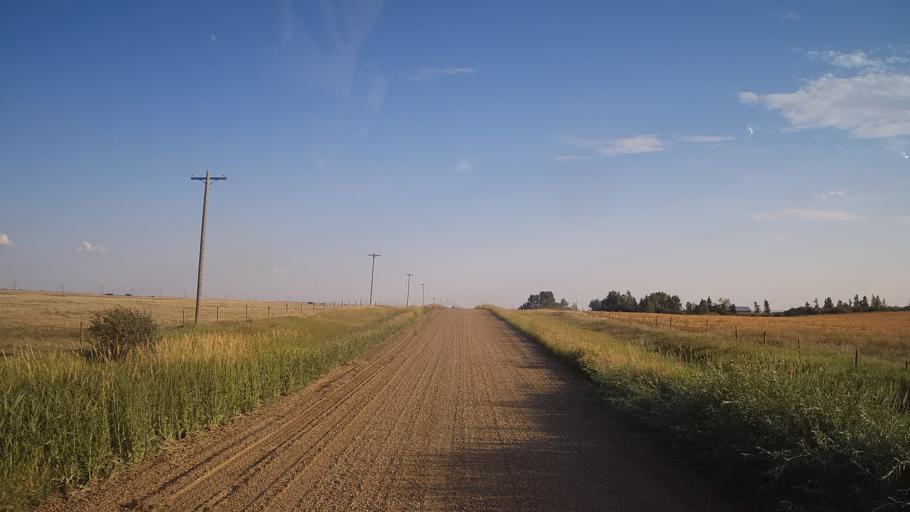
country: CA
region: Alberta
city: Hanna
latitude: 51.6158
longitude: -111.8569
